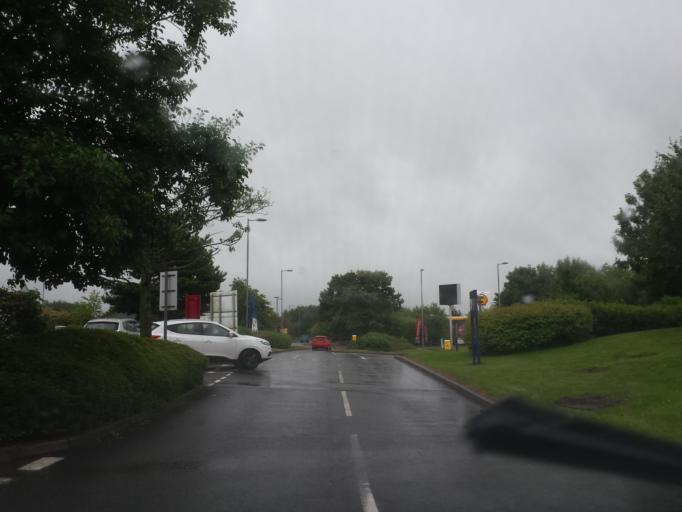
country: GB
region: England
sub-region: Derbyshire
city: Tibshelf
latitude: 53.1393
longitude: -1.3297
